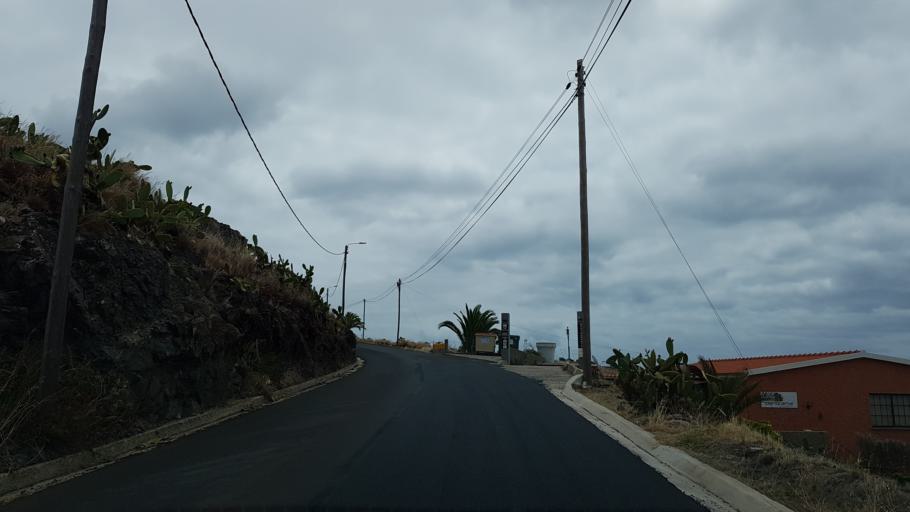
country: PT
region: Madeira
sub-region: Porto Santo
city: Vila de Porto Santo
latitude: 33.0692
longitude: -16.3211
